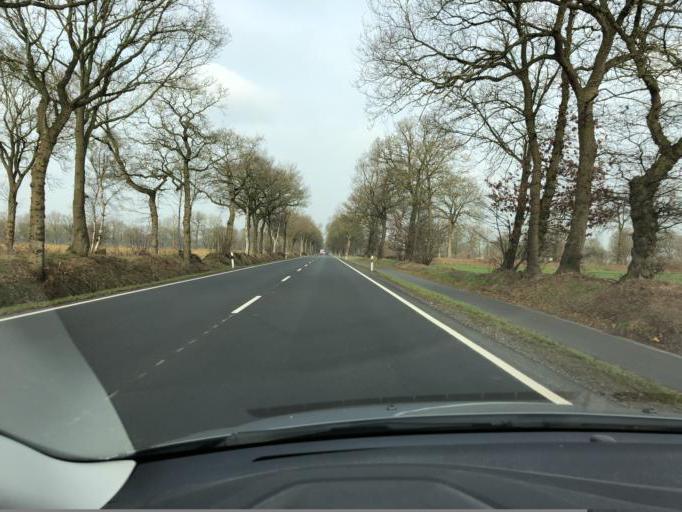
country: DE
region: Lower Saxony
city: Mittegrossefehn
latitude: 53.3622
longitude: 7.5943
